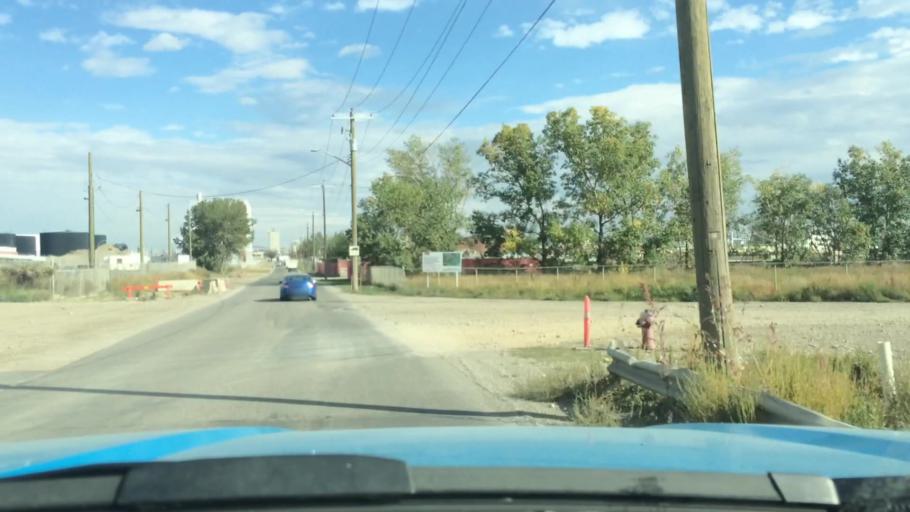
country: CA
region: Alberta
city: Calgary
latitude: 51.0087
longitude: -114.0251
